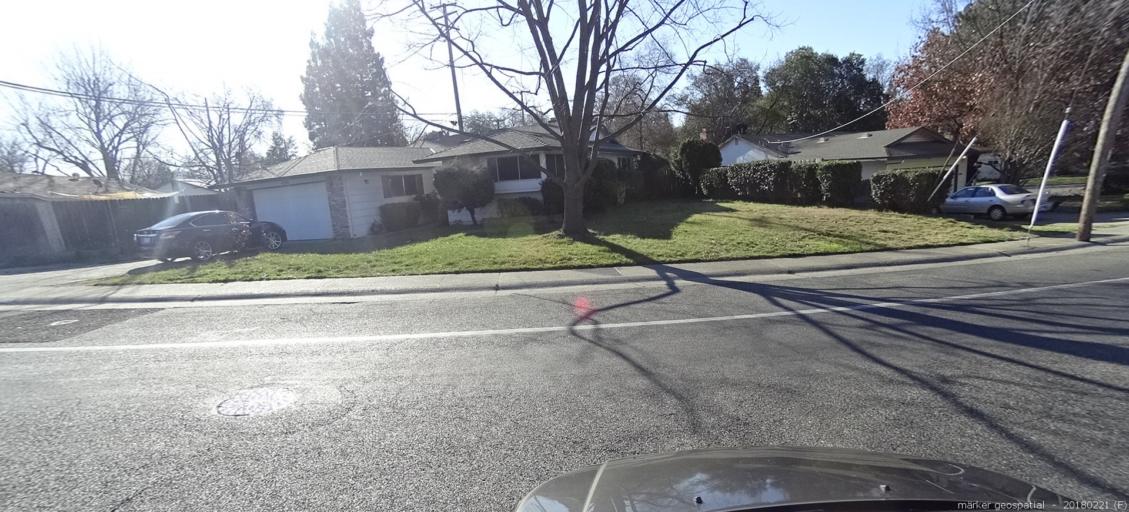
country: US
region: California
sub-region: Sacramento County
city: Orangevale
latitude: 38.6874
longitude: -121.2539
